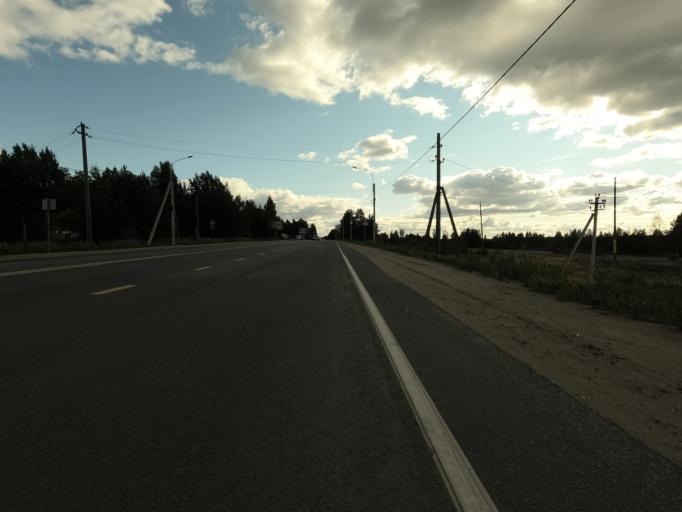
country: RU
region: Leningrad
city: Vsevolozhsk
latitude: 59.9853
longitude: 30.6554
